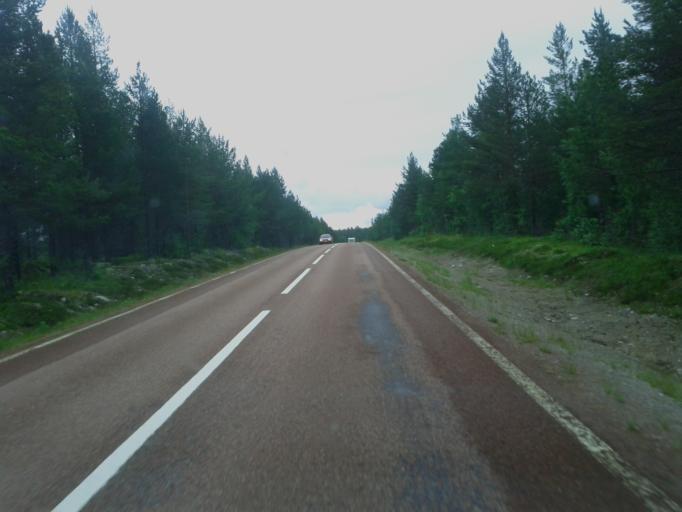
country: NO
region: Hedmark
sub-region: Engerdal
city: Engerdal
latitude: 61.8137
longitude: 12.3545
